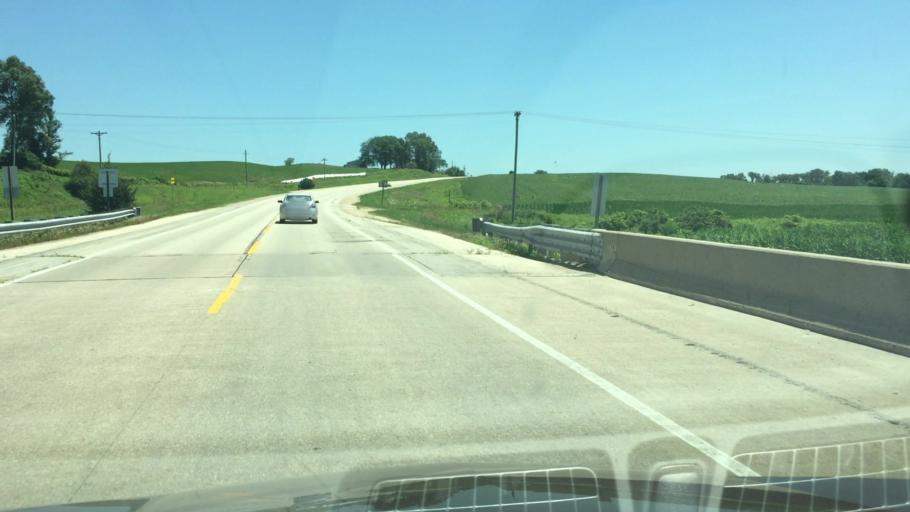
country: US
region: Iowa
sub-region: Jackson County
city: Maquoketa
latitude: 42.0729
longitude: -90.8018
